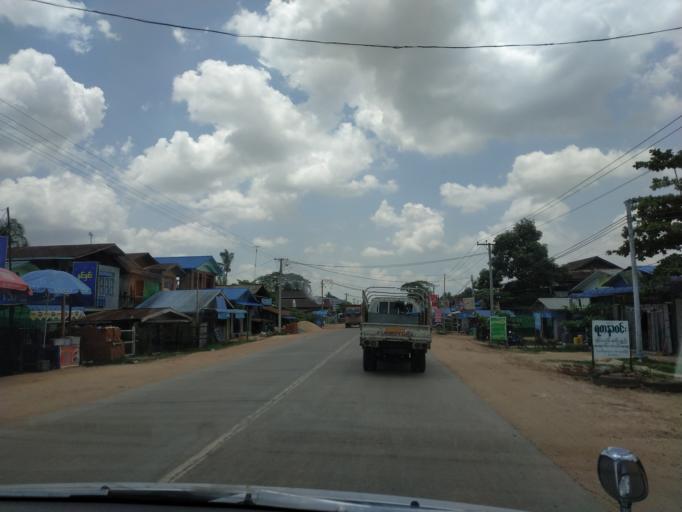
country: MM
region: Bago
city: Bago
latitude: 17.4753
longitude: 96.5240
